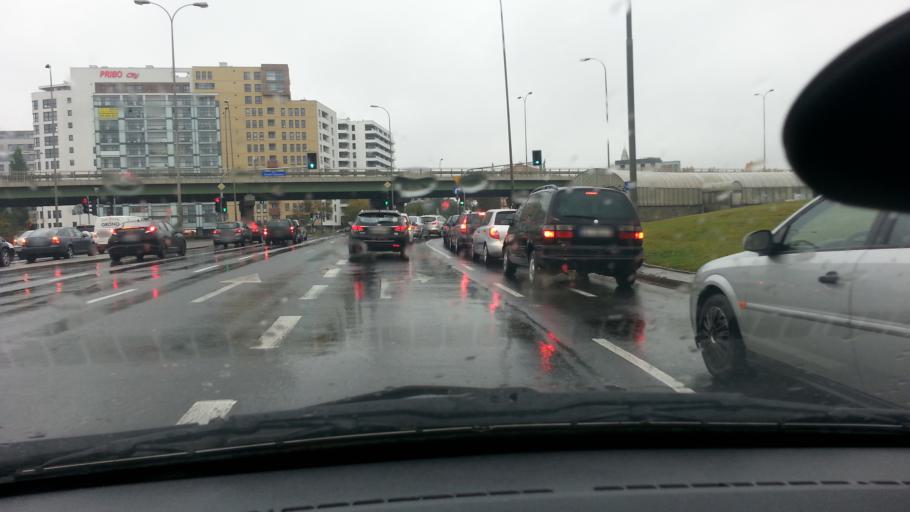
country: PL
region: Masovian Voivodeship
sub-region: Warszawa
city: Ochota
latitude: 52.2170
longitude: 20.9601
